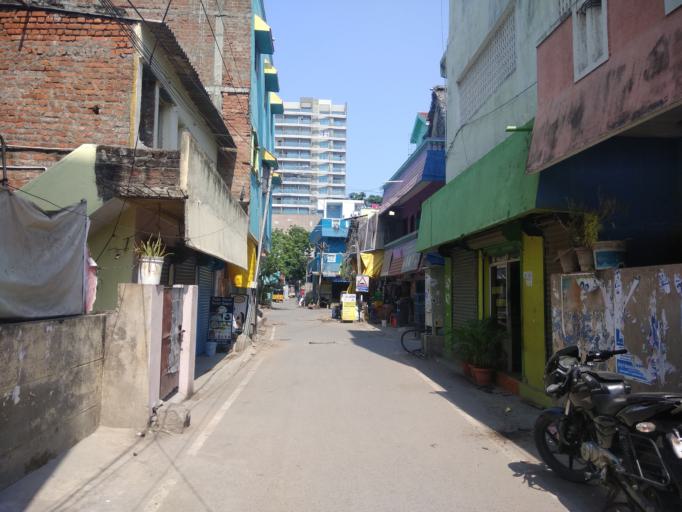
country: IN
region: Tamil Nadu
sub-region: Kancheepuram
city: Alandur
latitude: 12.9926
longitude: 80.2153
